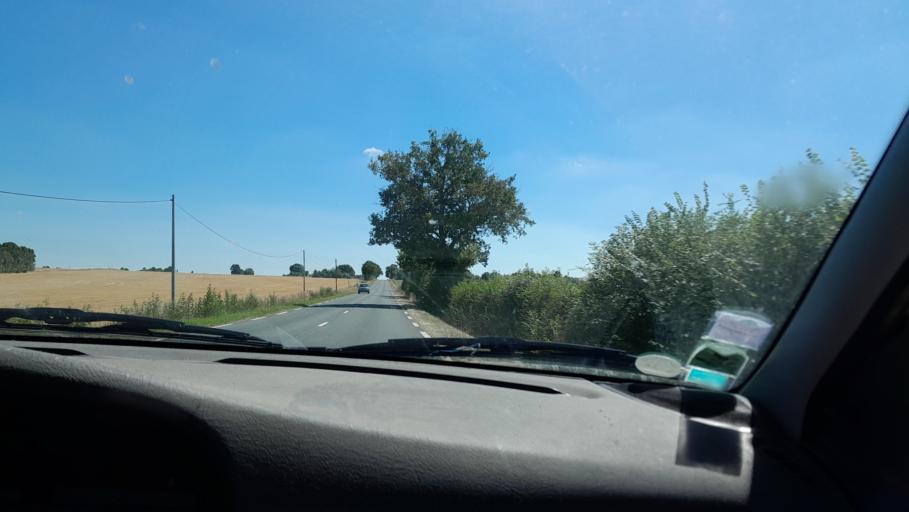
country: FR
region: Pays de la Loire
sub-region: Departement de la Loire-Atlantique
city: Saint-Mars-la-Jaille
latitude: 47.4788
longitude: -1.1742
